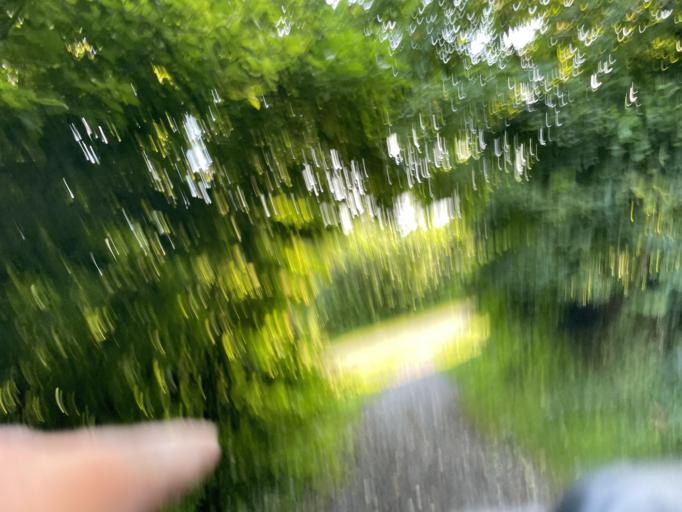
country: DE
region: North Rhine-Westphalia
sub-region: Regierungsbezirk Dusseldorf
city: Essen
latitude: 51.4039
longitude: 7.0522
